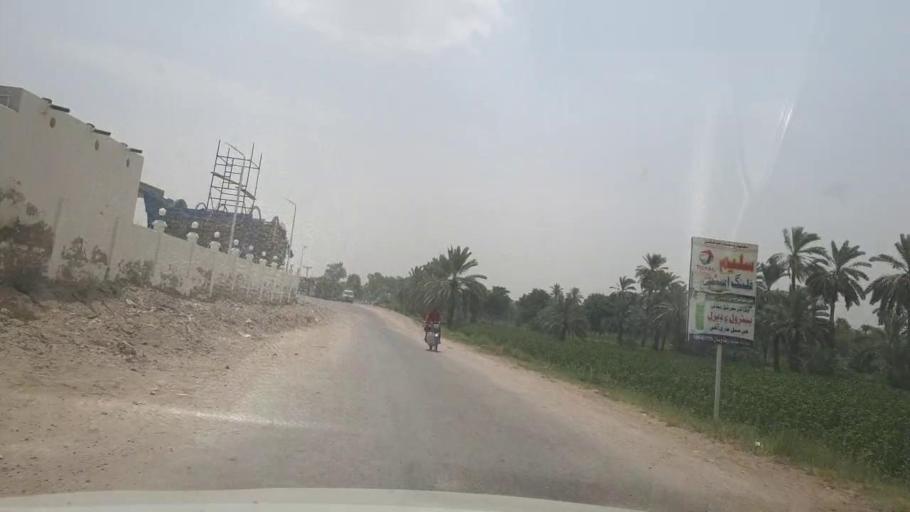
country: PK
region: Sindh
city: Kot Diji
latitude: 27.3689
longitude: 68.7231
